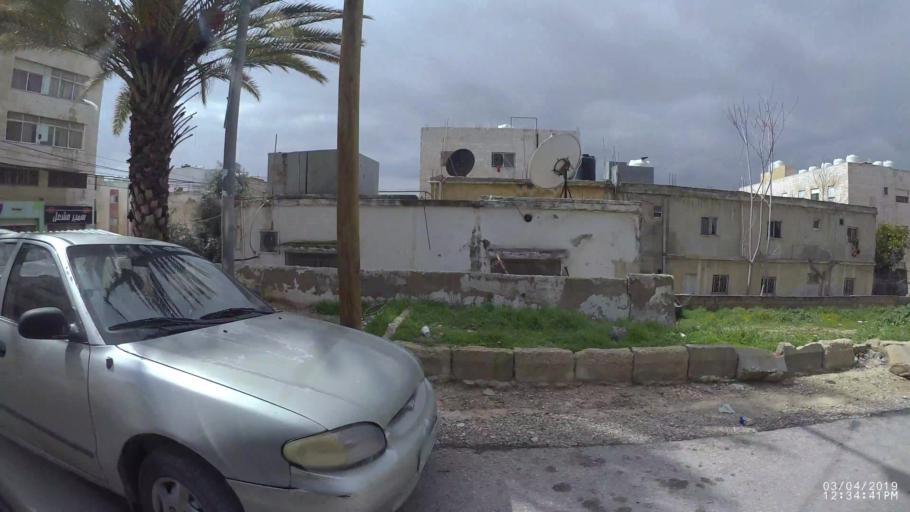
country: JO
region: Amman
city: Wadi as Sir
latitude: 31.9595
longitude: 35.8360
